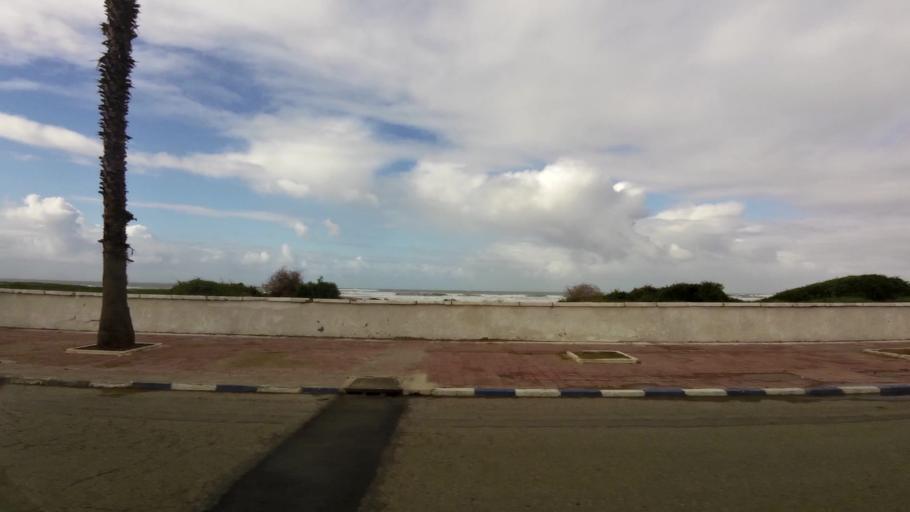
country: MA
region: Doukkala-Abda
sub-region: El-Jadida
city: El Jadida
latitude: 33.2442
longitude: -8.4762
